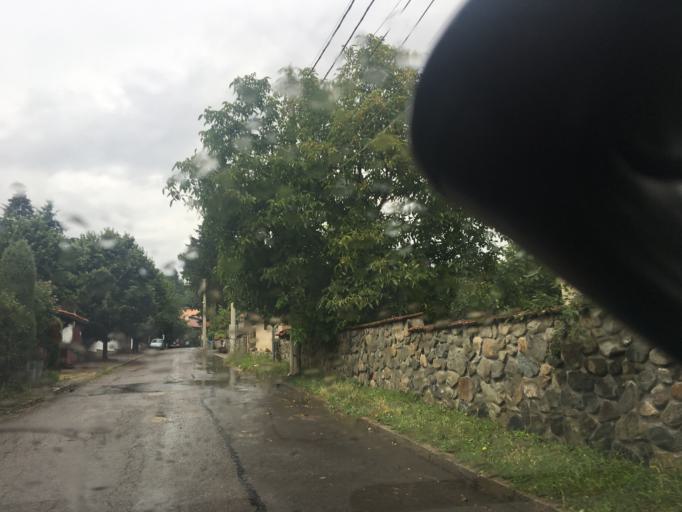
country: BG
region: Sofia-Capital
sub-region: Stolichna Obshtina
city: Sofia
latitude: 42.5856
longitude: 23.3523
